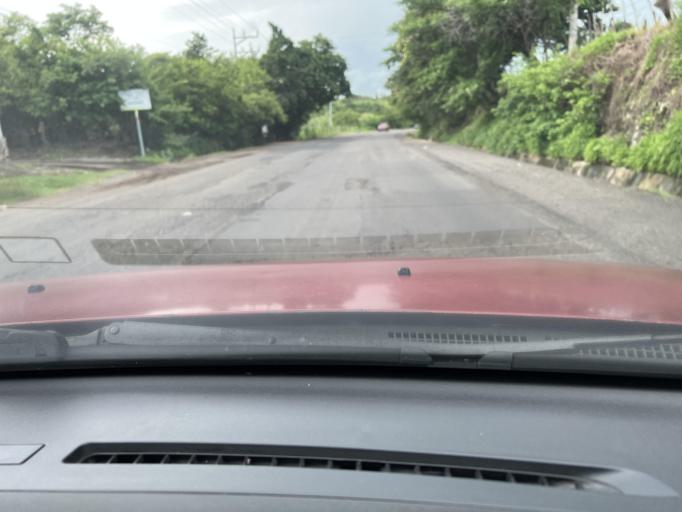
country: SV
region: La Union
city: San Alejo
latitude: 13.3978
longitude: -87.8989
